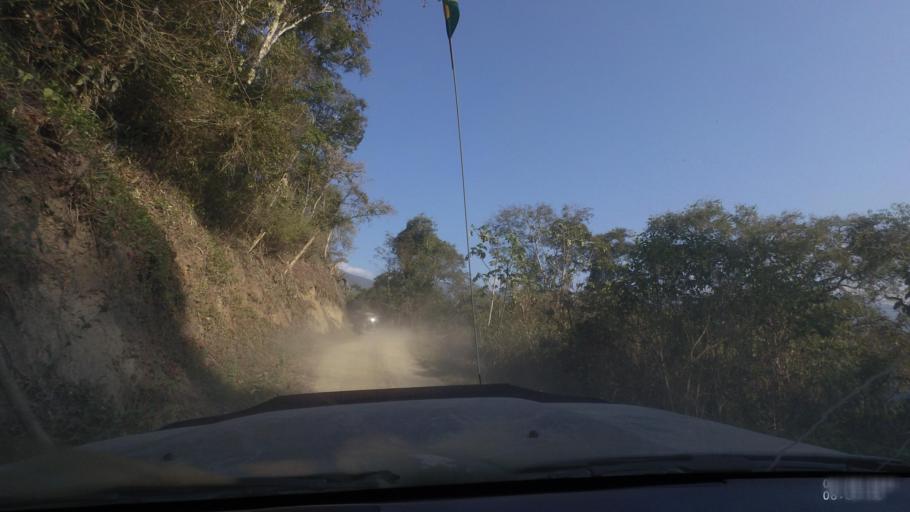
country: BO
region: La Paz
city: Quime
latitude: -16.5141
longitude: -66.7645
